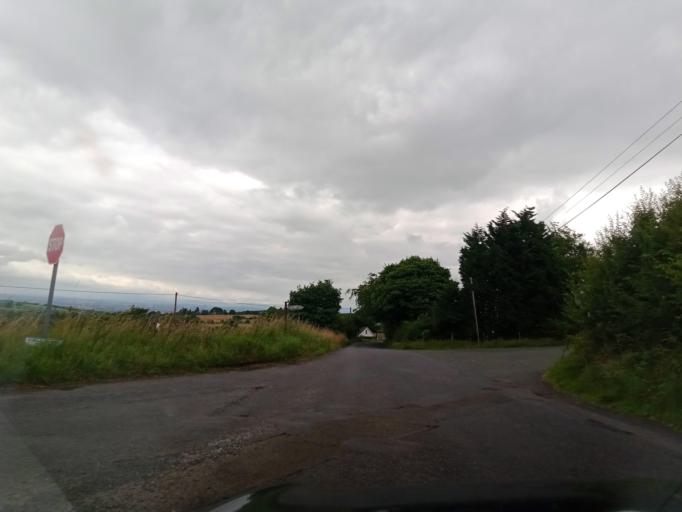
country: IE
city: Ballylinan
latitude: 52.8984
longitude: -7.1180
